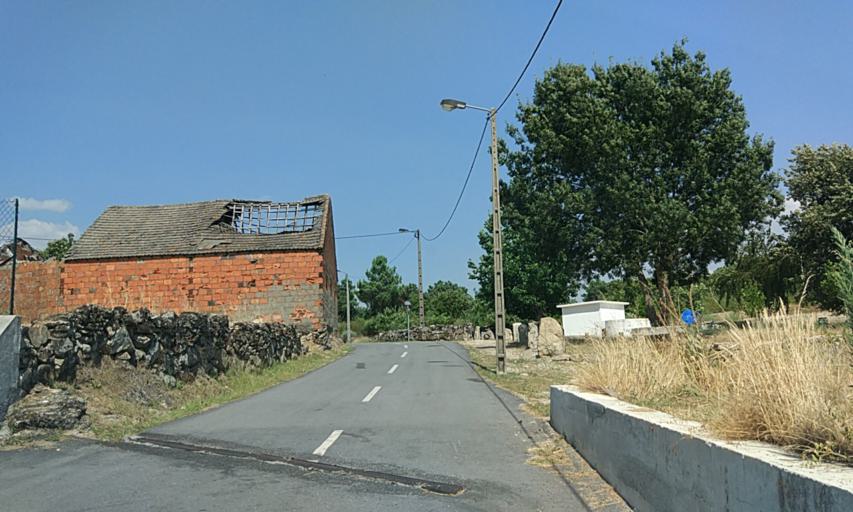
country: PT
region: Vila Real
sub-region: Murca
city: Murca
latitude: 41.3470
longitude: -7.4806
